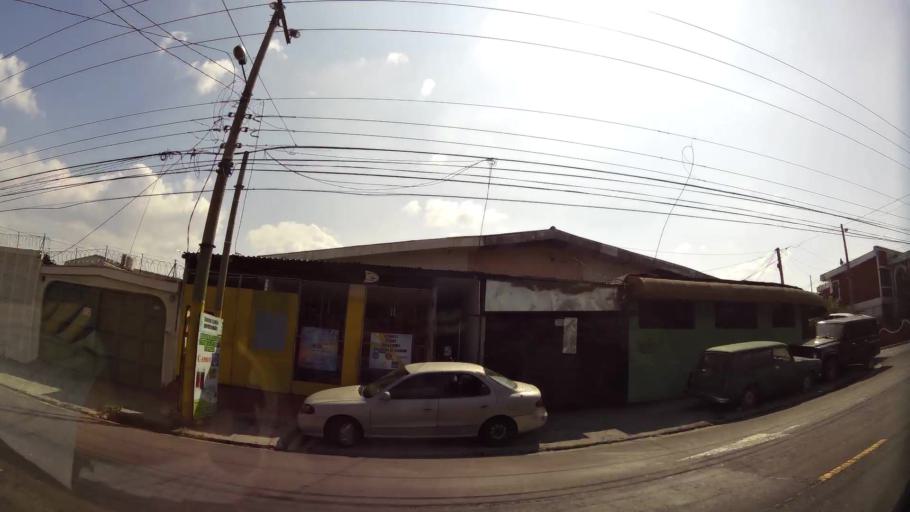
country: SV
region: San Salvador
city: Mejicanos
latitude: 13.7230
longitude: -89.2193
